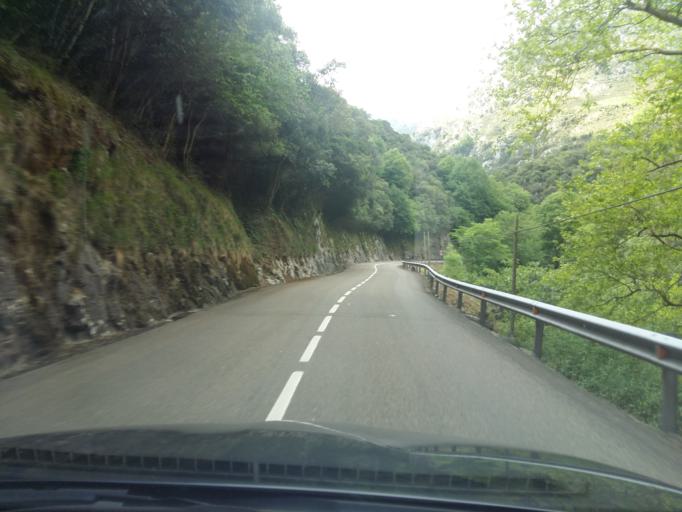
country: ES
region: Cantabria
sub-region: Provincia de Cantabria
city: Tresviso
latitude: 43.3124
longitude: -4.6088
